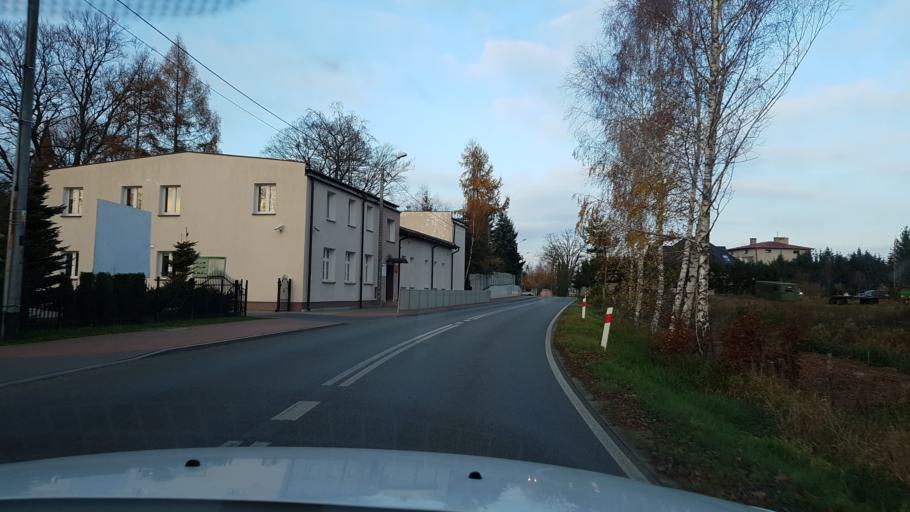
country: PL
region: West Pomeranian Voivodeship
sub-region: Koszalin
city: Koszalin
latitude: 54.1197
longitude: 16.1672
